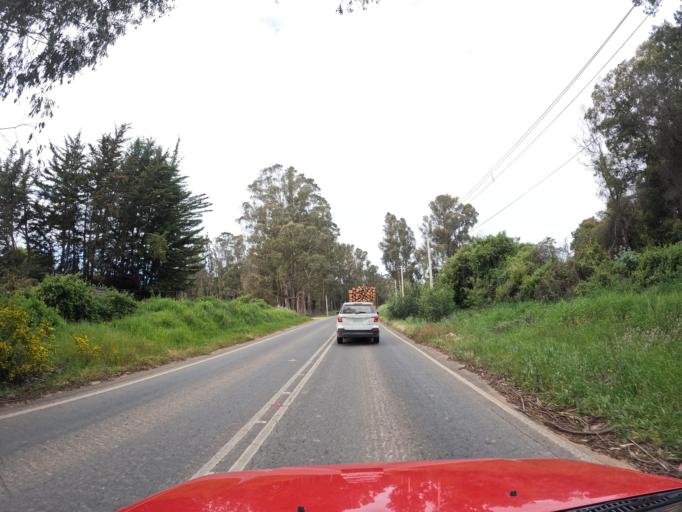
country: CL
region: O'Higgins
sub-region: Provincia de Colchagua
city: Santa Cruz
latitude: -34.3578
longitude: -71.8846
